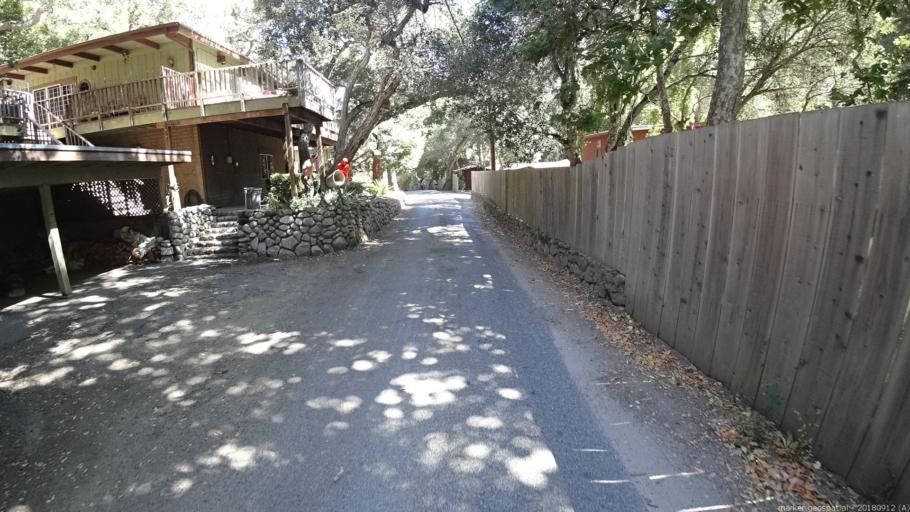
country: US
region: California
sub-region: Monterey County
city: Carmel Valley Village
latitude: 36.4602
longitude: -121.7286
